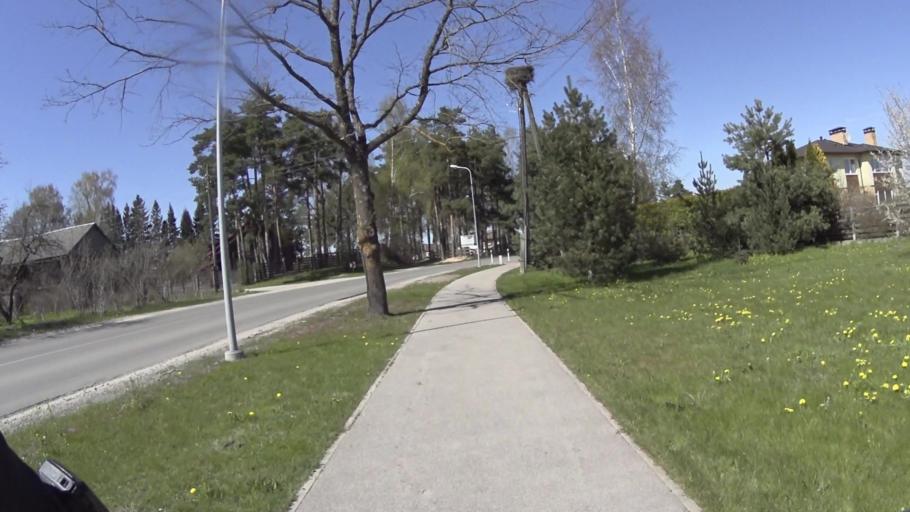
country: LV
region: Babite
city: Pinki
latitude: 56.9750
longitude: 23.9687
